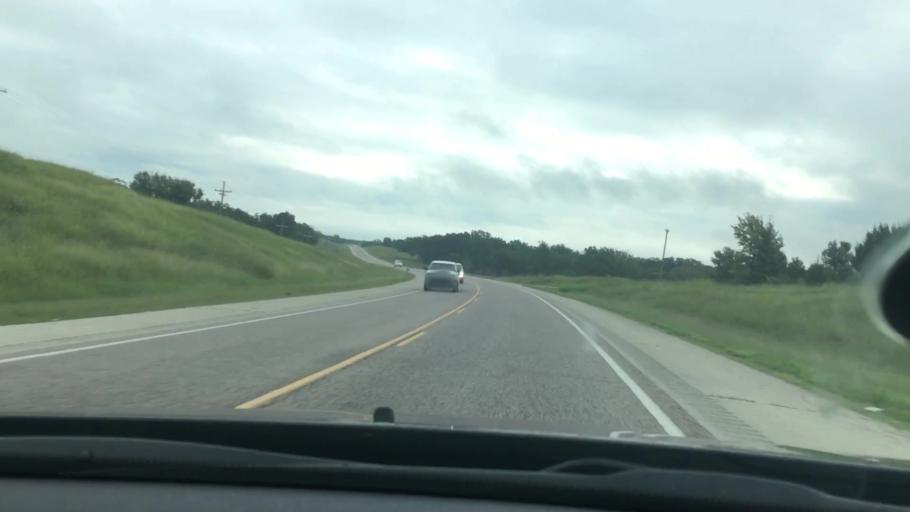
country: US
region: Oklahoma
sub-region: Pontotoc County
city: Ada
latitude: 34.7880
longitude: -96.5664
